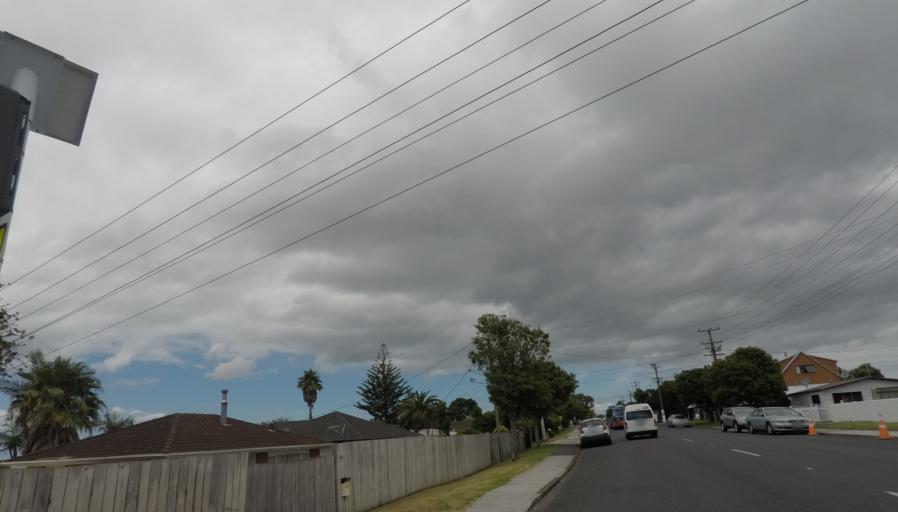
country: NZ
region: Auckland
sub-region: Auckland
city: Rosebank
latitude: -36.8460
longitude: 174.6157
